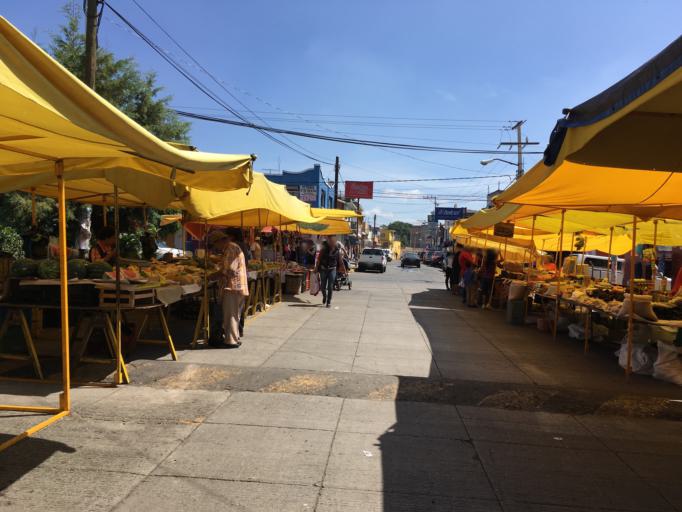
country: MX
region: Michoacan
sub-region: Morelia
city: Morelos
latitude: 19.6491
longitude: -101.2393
